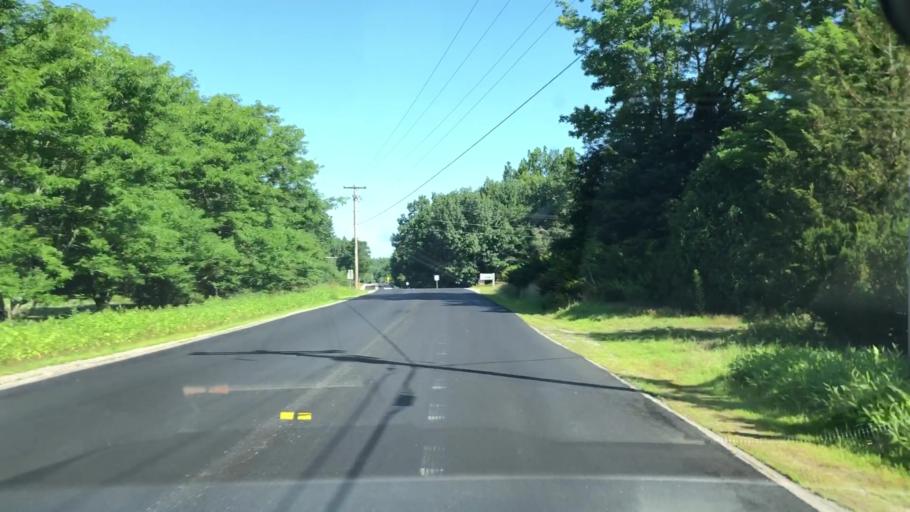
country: US
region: New Hampshire
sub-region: Hillsborough County
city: Milford
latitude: 42.8269
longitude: -71.6076
